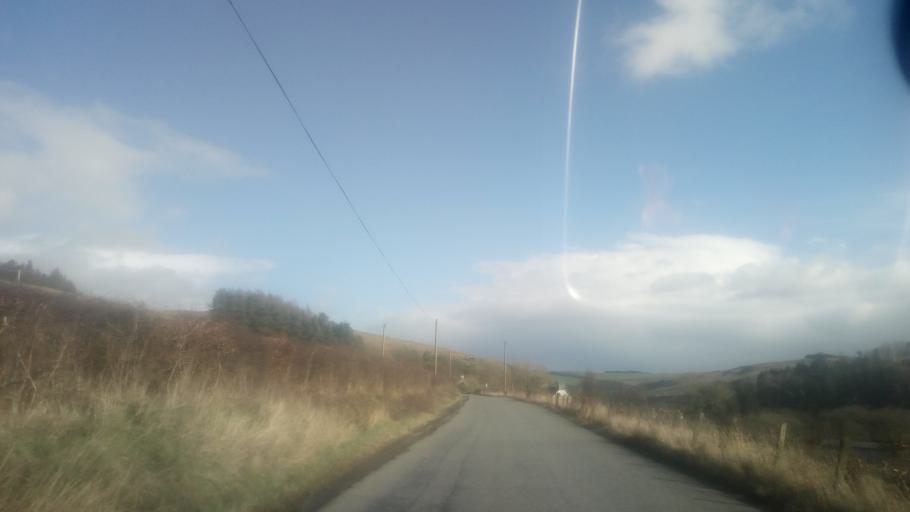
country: GB
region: Scotland
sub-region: The Scottish Borders
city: Hawick
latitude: 55.4179
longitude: -2.8636
